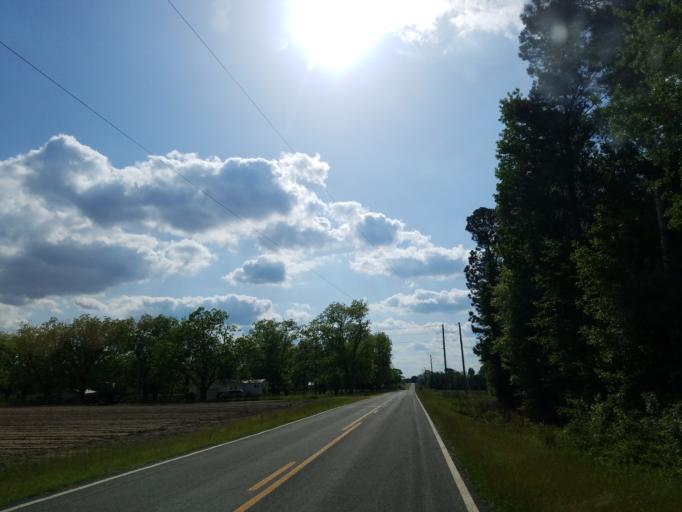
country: US
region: Georgia
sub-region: Dooly County
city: Vienna
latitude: 32.1528
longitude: -83.7849
